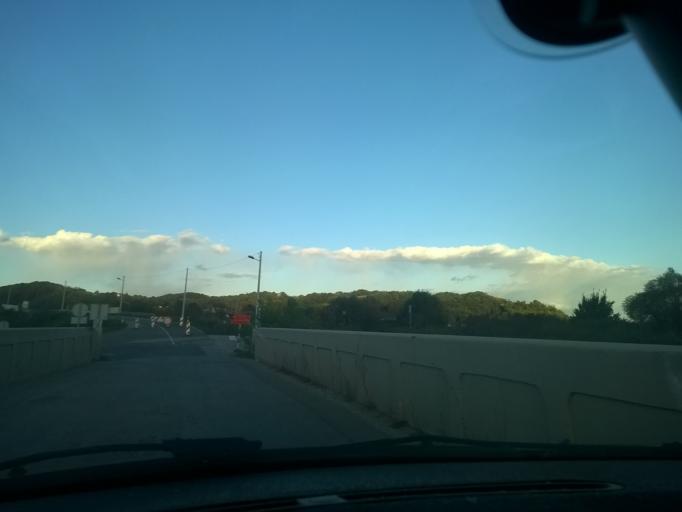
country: HR
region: Krapinsko-Zagorska
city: Zabok
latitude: 46.0189
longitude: 15.8562
